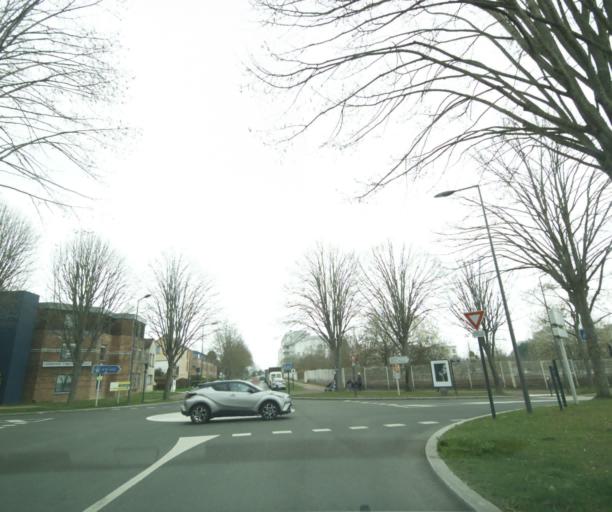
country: FR
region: Ile-de-France
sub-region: Departement du Val-d'Oise
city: Vaureal
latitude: 49.0509
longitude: 2.0318
